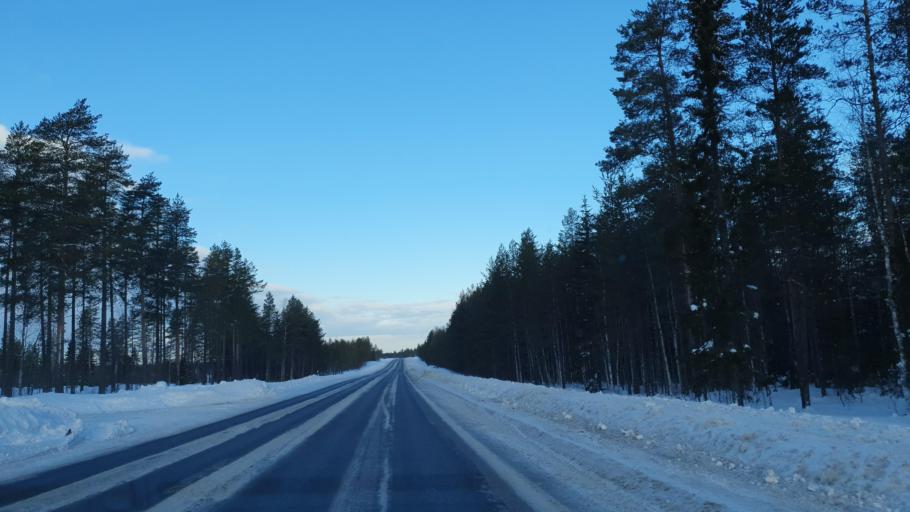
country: FI
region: Kainuu
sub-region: Kajaani
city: Vaala
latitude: 64.5722
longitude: 26.8561
